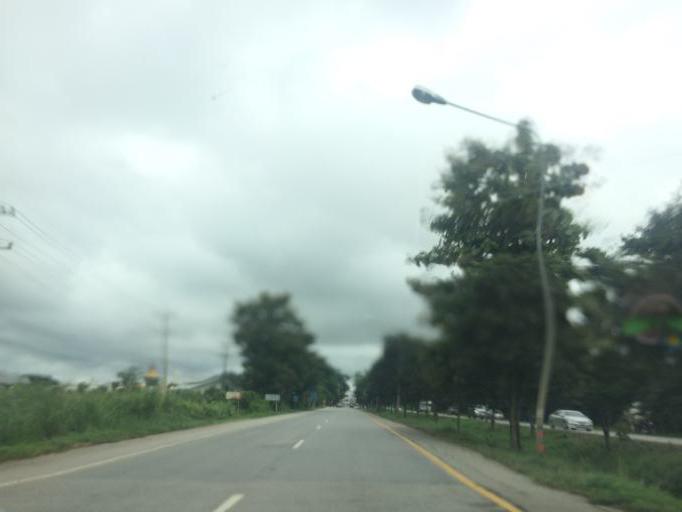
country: TH
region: Chiang Rai
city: Mae Lao
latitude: 19.8190
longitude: 99.7615
